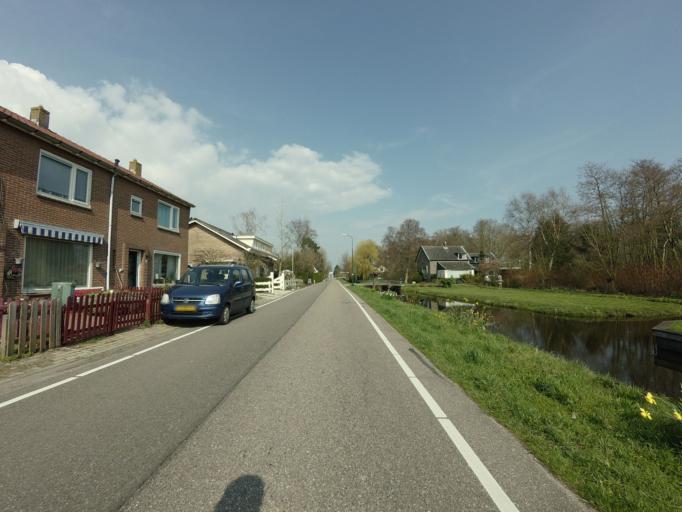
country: NL
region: North Holland
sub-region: Gemeente Wijdemeren
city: Kortenhoef
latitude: 52.2720
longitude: 5.1047
